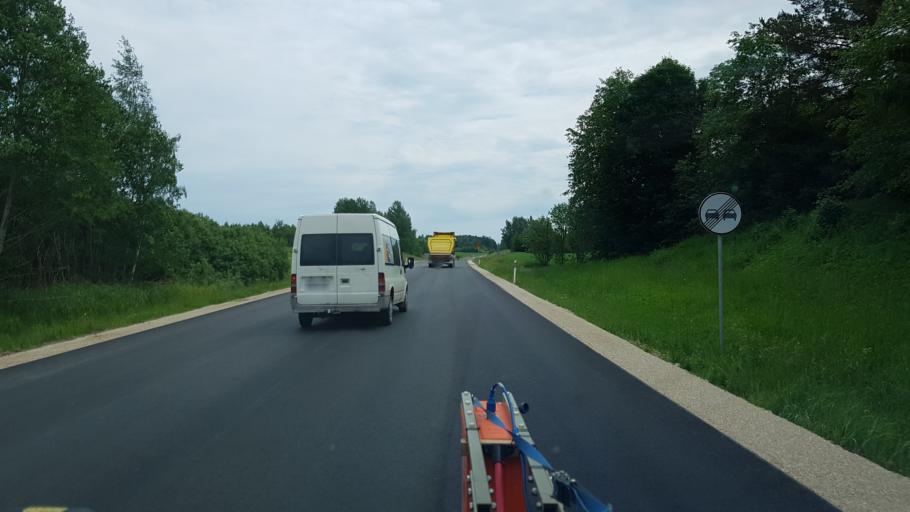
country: EE
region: Vorumaa
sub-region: Voru linn
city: Voru
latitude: 57.7620
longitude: 27.2012
